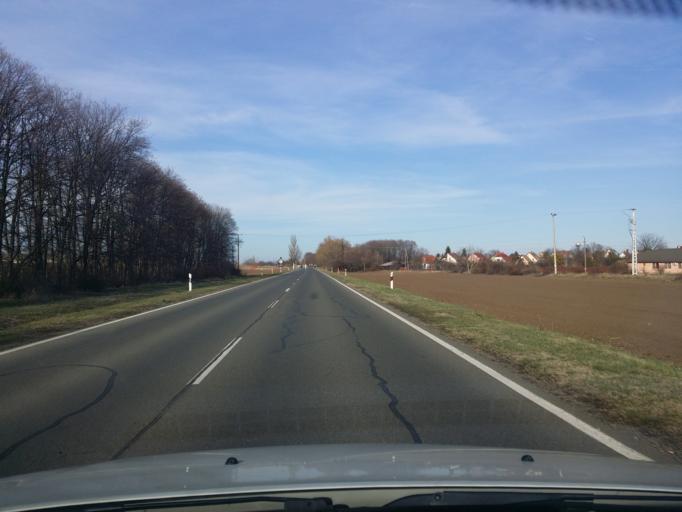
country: HU
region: Tolna
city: Dunaszentgyorgy
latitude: 46.5237
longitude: 18.8035
